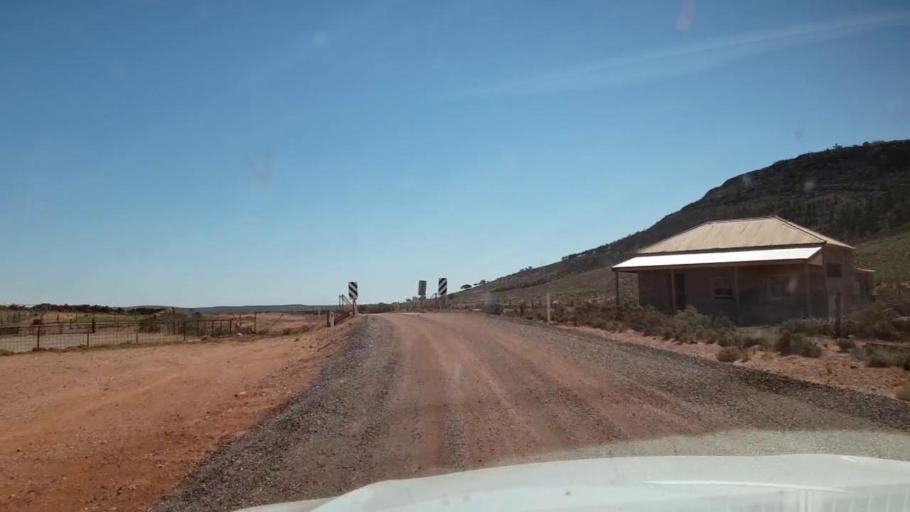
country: AU
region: South Australia
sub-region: Whyalla
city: Whyalla
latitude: -32.6853
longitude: 137.1246
